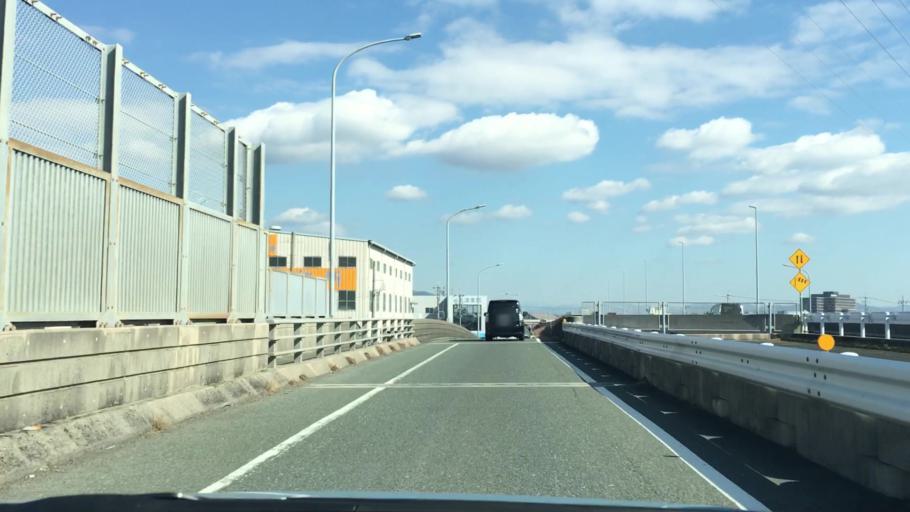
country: JP
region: Aichi
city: Kozakai-cho
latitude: 34.8251
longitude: 137.3374
